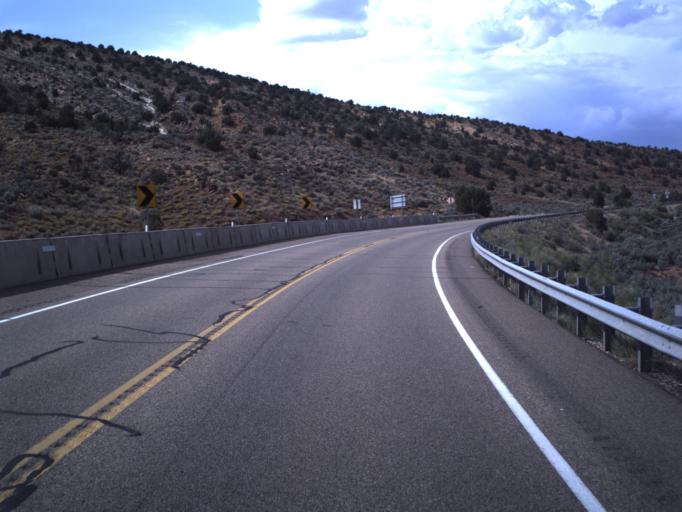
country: US
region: Utah
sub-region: Kane County
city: Kanab
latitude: 37.1251
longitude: -111.9762
